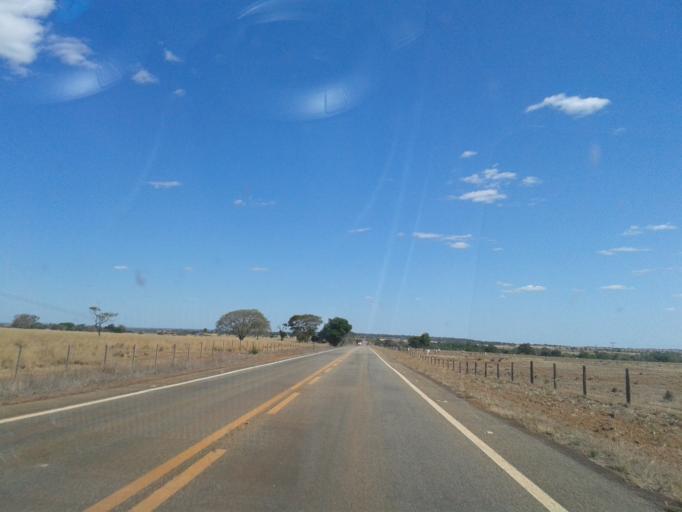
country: BR
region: Goias
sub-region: Sao Miguel Do Araguaia
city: Sao Miguel do Araguaia
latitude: -13.4298
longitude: -50.2804
